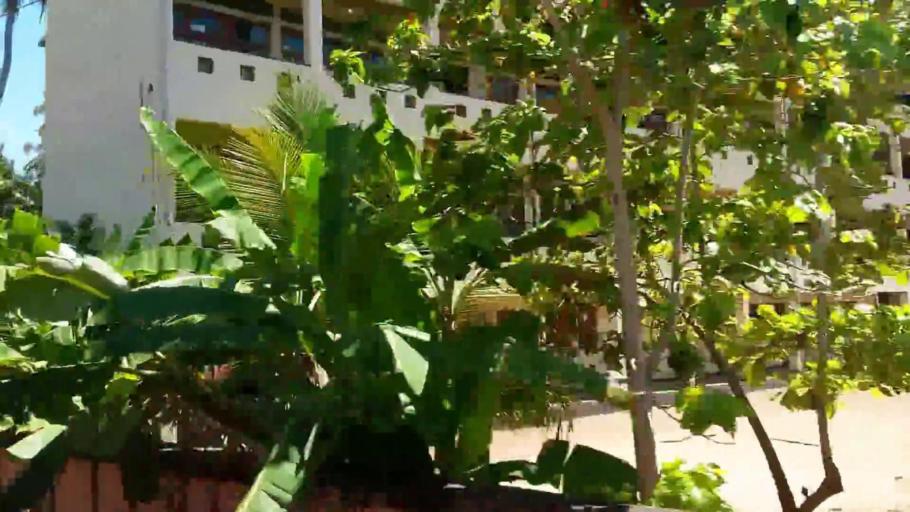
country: LK
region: Southern
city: Hikkaduwa
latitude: 6.1739
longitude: 80.0840
